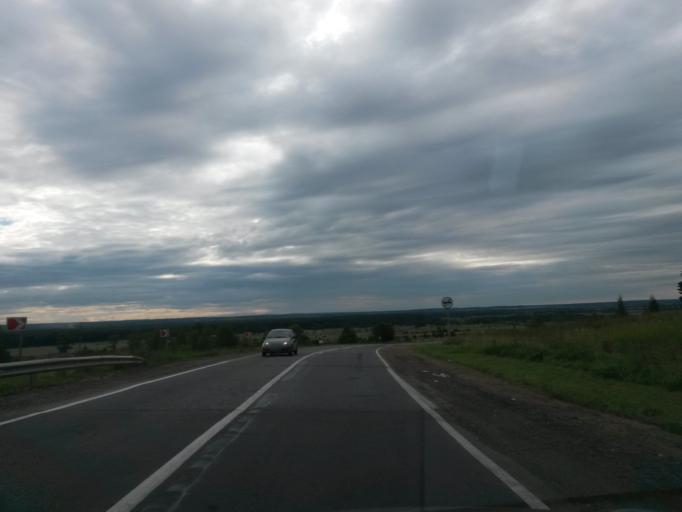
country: RU
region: Jaroslavl
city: Gavrilov-Yam
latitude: 57.3598
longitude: 39.7772
